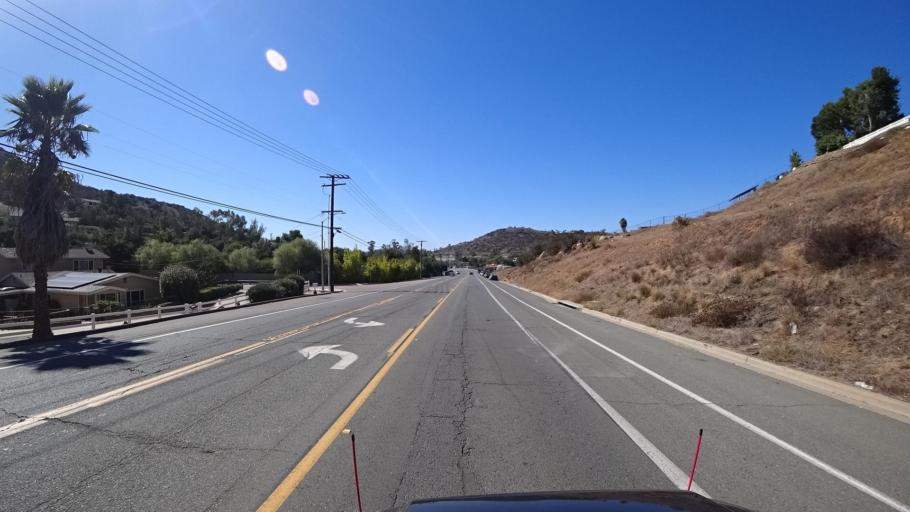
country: US
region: California
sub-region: San Diego County
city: Crest
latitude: 32.8479
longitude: -116.8659
